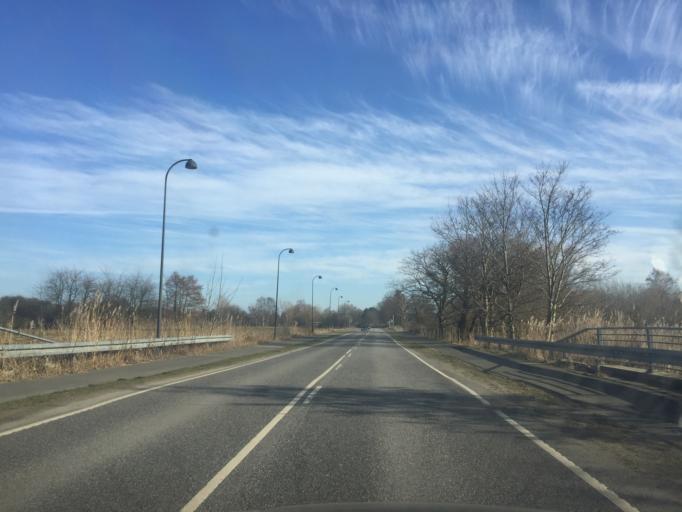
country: DK
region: Capital Region
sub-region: Rudersdal Kommune
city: Trorod
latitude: 55.8505
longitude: 12.5535
